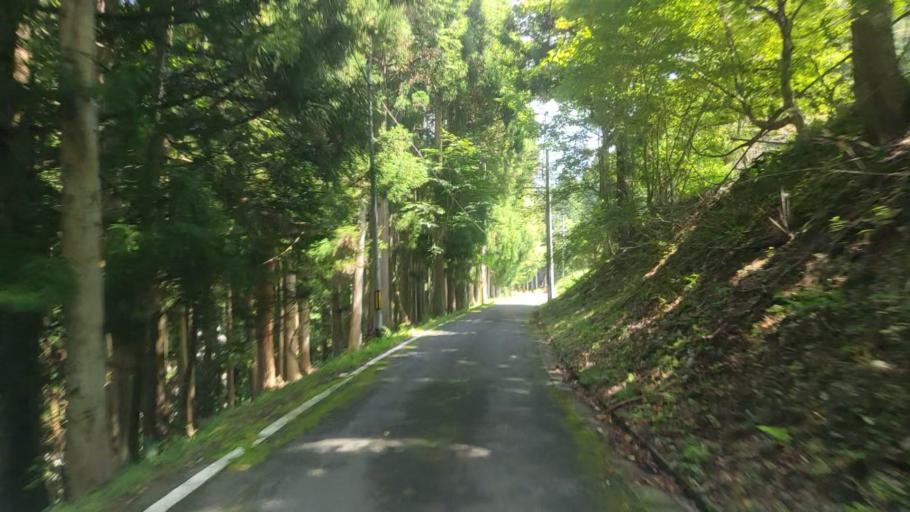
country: JP
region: Fukui
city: Ono
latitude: 35.7085
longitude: 136.5850
